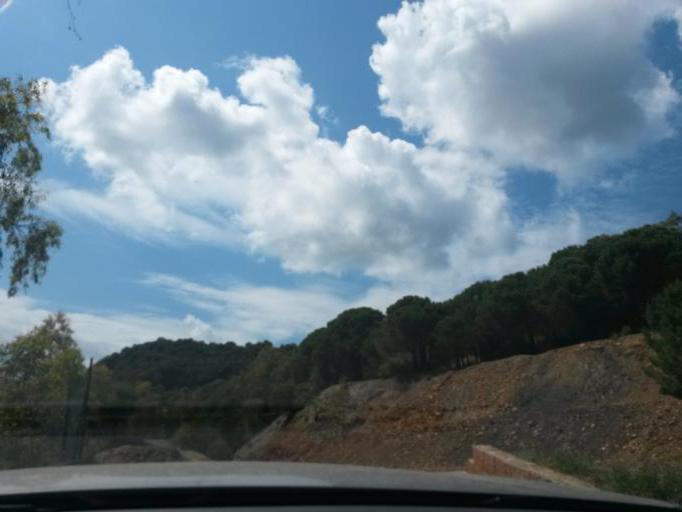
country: IT
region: Tuscany
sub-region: Provincia di Livorno
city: Rio Marina
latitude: 42.8156
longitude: 10.4243
